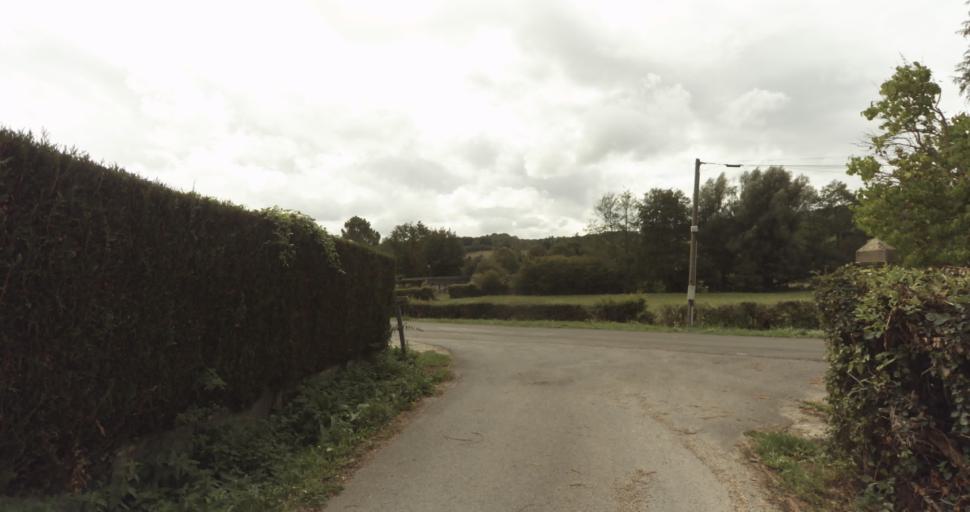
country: FR
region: Lower Normandy
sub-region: Departement de l'Orne
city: Gace
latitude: 48.8320
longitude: 0.2786
